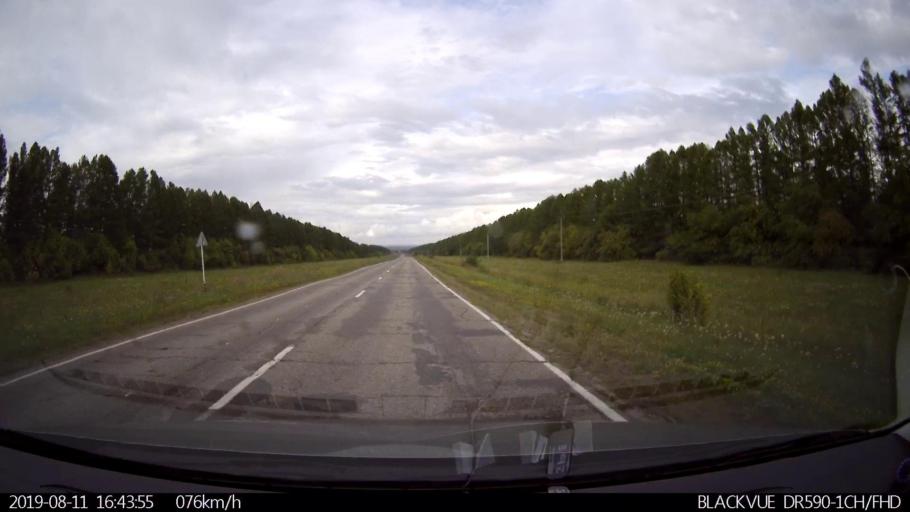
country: RU
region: Ulyanovsk
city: Mayna
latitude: 54.1737
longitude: 47.6766
